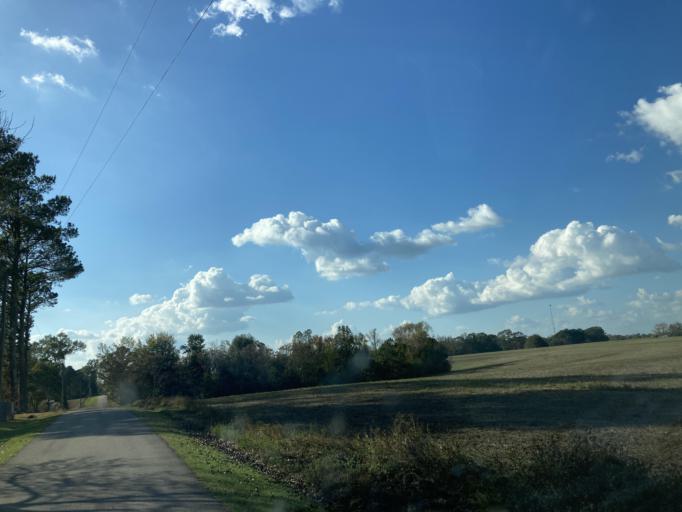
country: US
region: Mississippi
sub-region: Lamar County
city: Sumrall
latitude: 31.4339
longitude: -89.6383
